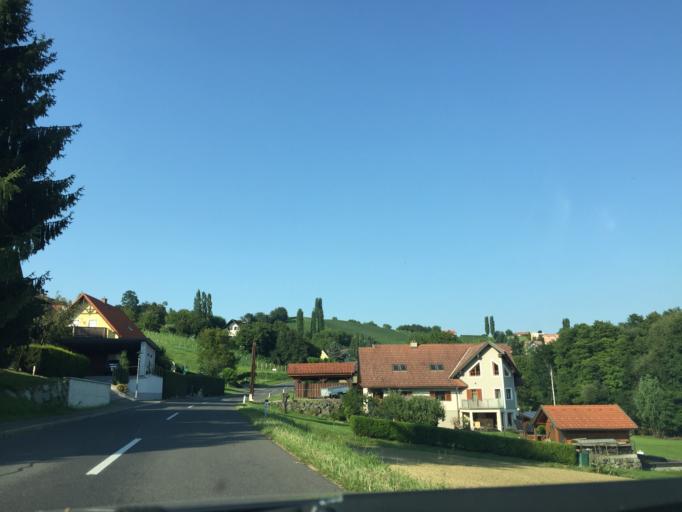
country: AT
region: Styria
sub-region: Politischer Bezirk Suedoststeiermark
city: Straden
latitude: 46.8066
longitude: 15.8617
